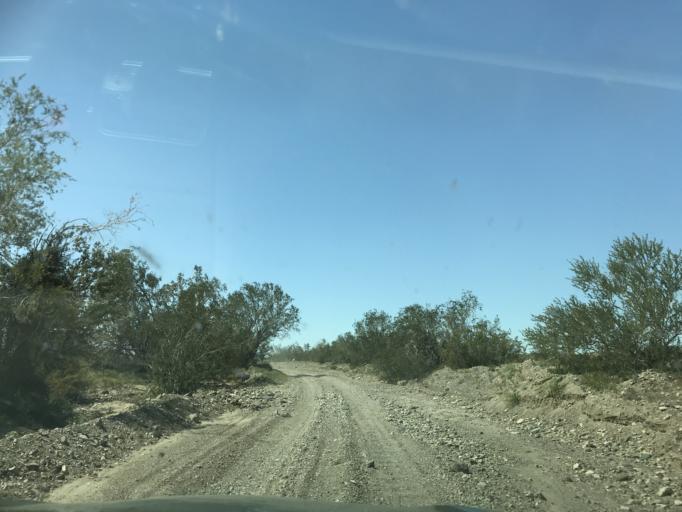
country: US
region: California
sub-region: Riverside County
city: Mesa Verde
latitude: 33.4756
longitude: -114.9455
